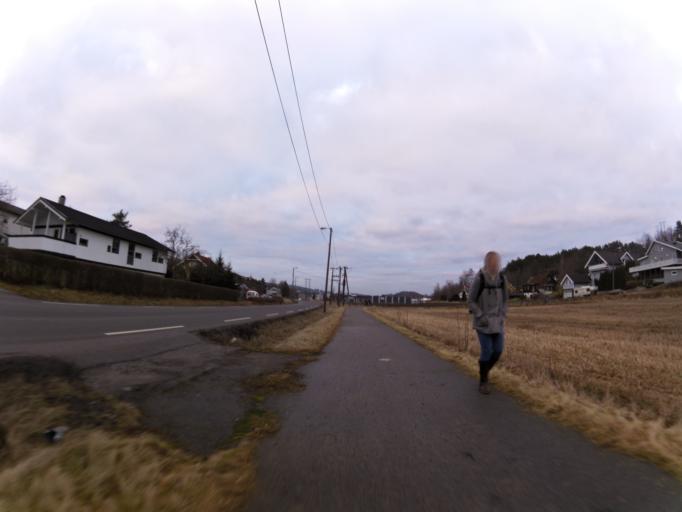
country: NO
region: Ostfold
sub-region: Fredrikstad
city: Fredrikstad
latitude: 59.2016
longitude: 10.8876
